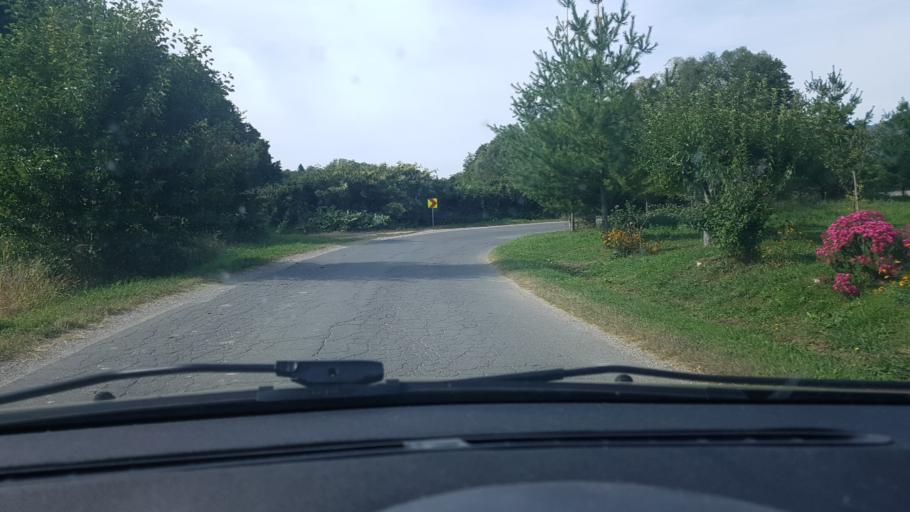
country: HR
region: Krapinsko-Zagorska
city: Zlatar
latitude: 46.1142
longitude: 16.1151
